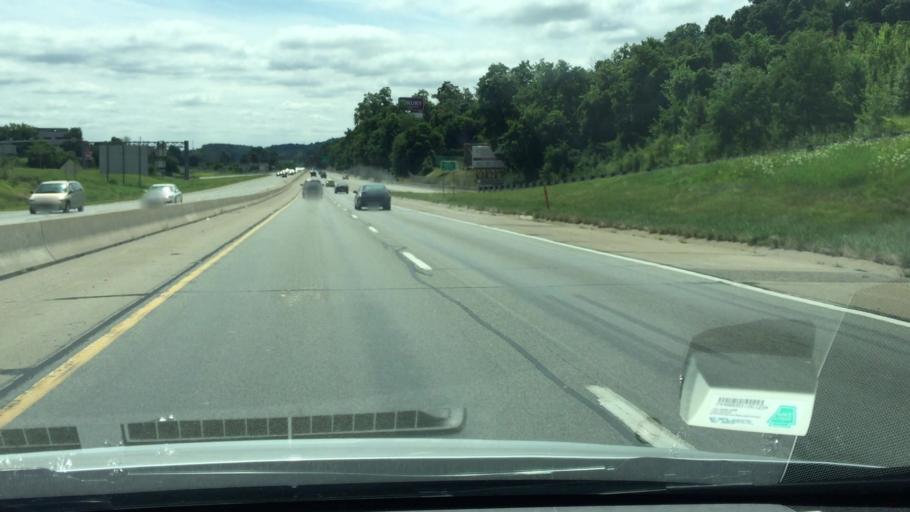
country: US
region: Pennsylvania
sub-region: Allegheny County
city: Rennerdale
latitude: 40.4369
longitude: -80.1512
